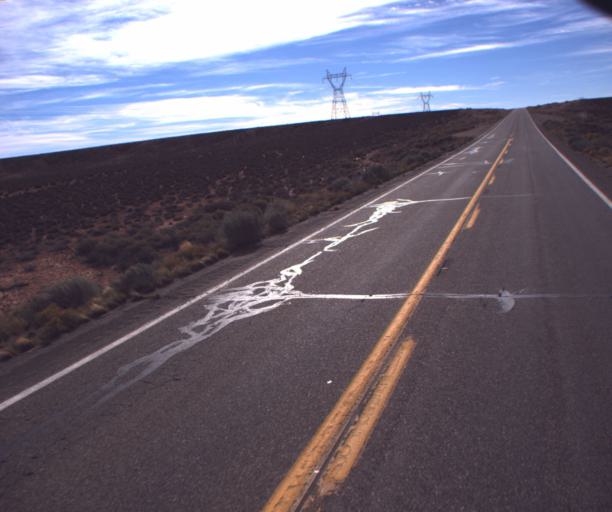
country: US
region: Arizona
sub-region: Coconino County
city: LeChee
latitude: 36.8037
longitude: -111.3048
